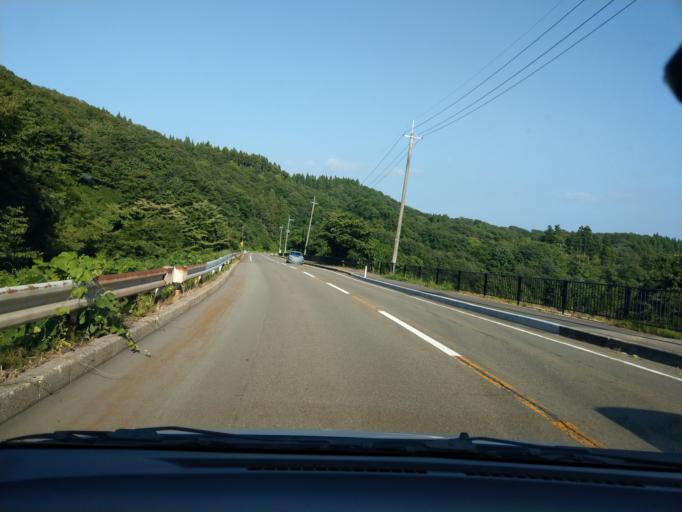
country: JP
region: Akita
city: Akita
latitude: 39.6066
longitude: 140.2029
